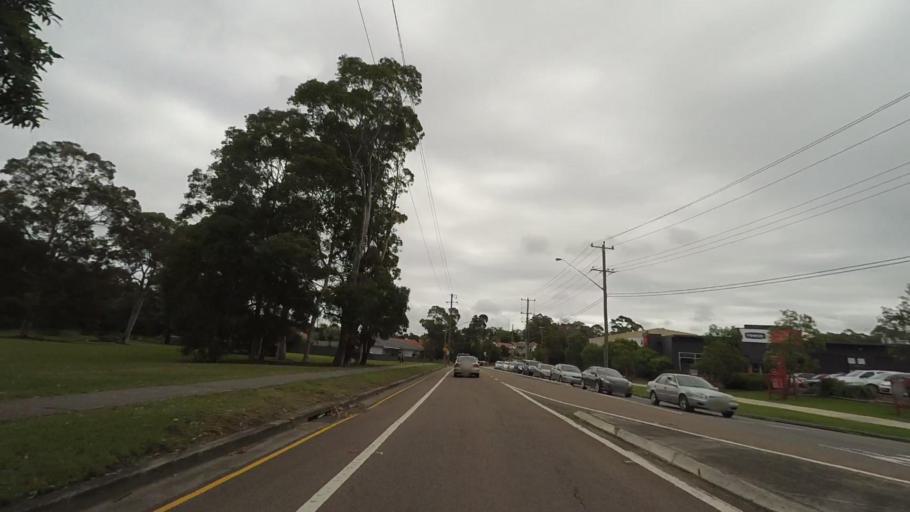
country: AU
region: New South Wales
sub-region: Lake Macquarie Shire
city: Highfields
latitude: -32.9414
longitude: 151.7059
